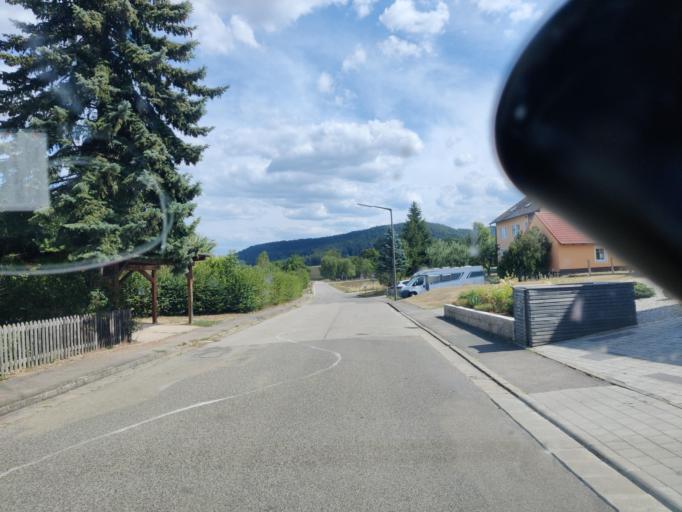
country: DE
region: Bavaria
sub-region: Regierungsbezirk Mittelfranken
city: Bergen
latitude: 49.0990
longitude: 11.1370
